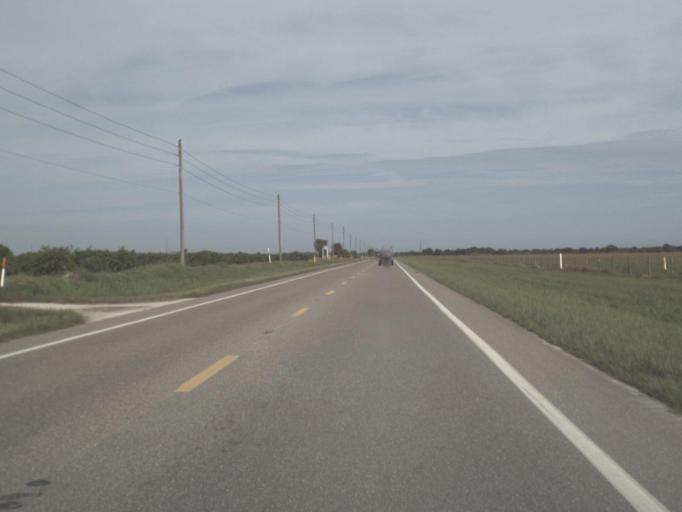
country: US
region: Florida
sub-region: DeSoto County
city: Nocatee
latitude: 27.0239
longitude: -81.7645
